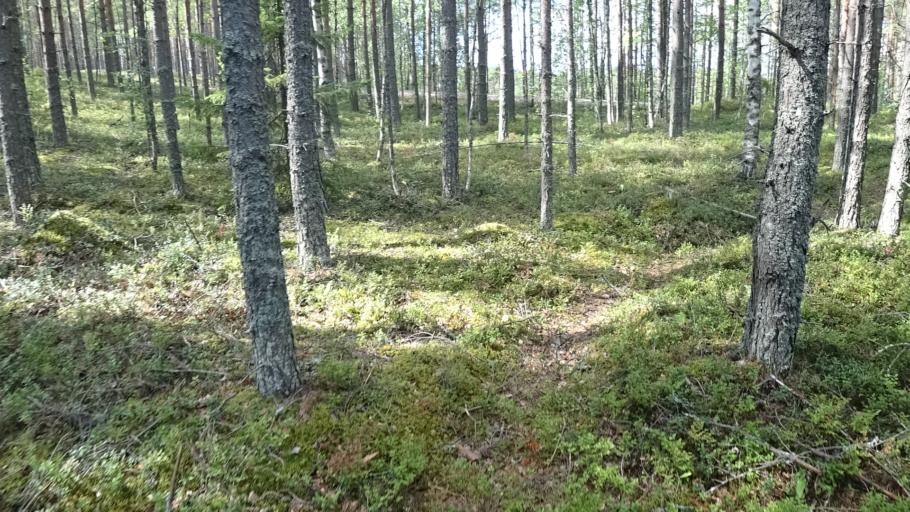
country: FI
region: North Karelia
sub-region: Joensuu
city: Ilomantsi
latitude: 62.6084
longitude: 31.1862
